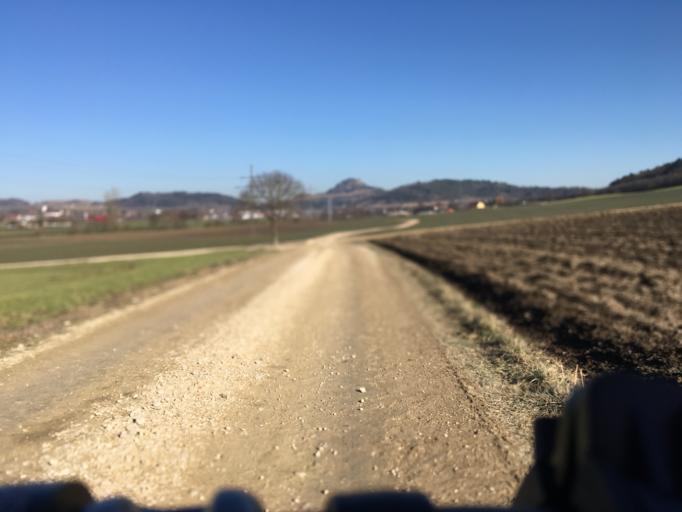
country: DE
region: Baden-Wuerttemberg
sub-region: Freiburg Region
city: Hilzingen
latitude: 47.7552
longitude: 8.7664
